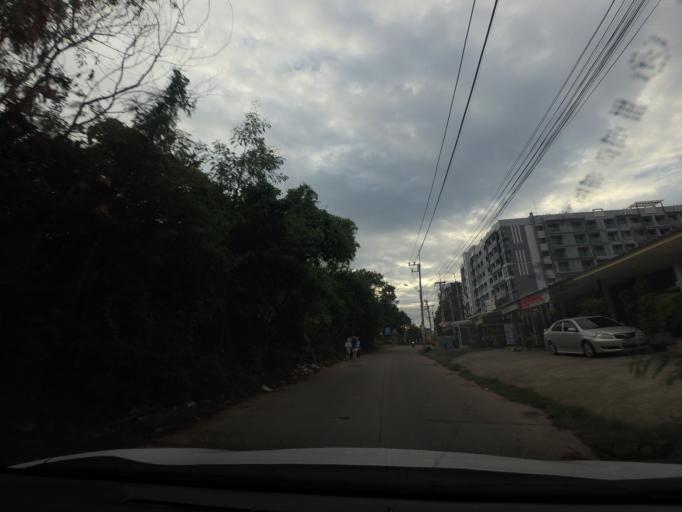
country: TH
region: Chon Buri
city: Phatthaya
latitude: 12.8991
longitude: 100.8813
